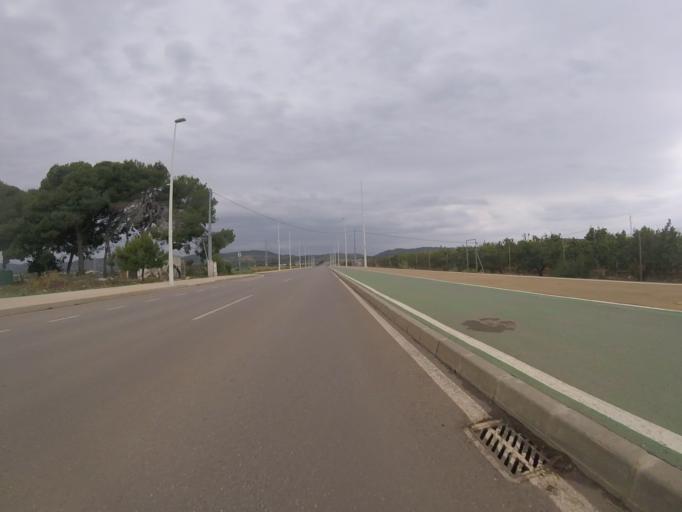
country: ES
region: Valencia
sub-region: Provincia de Castello
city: Torreblanca
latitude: 40.2212
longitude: 0.2148
